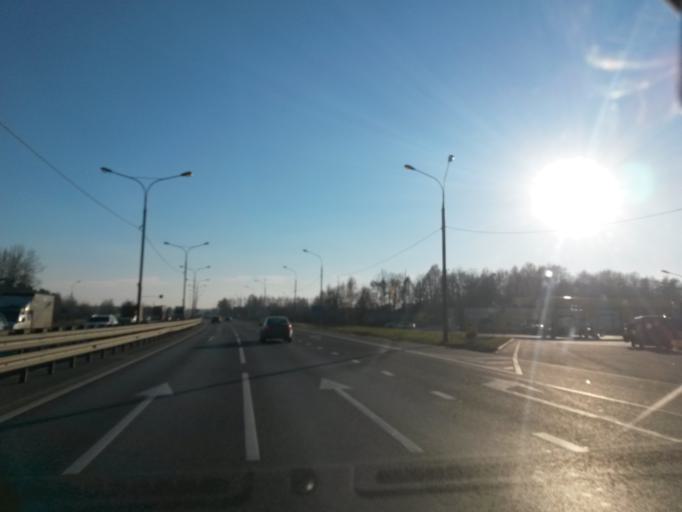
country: RU
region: Moskovskaya
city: Pushkino
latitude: 56.0106
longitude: 37.8774
